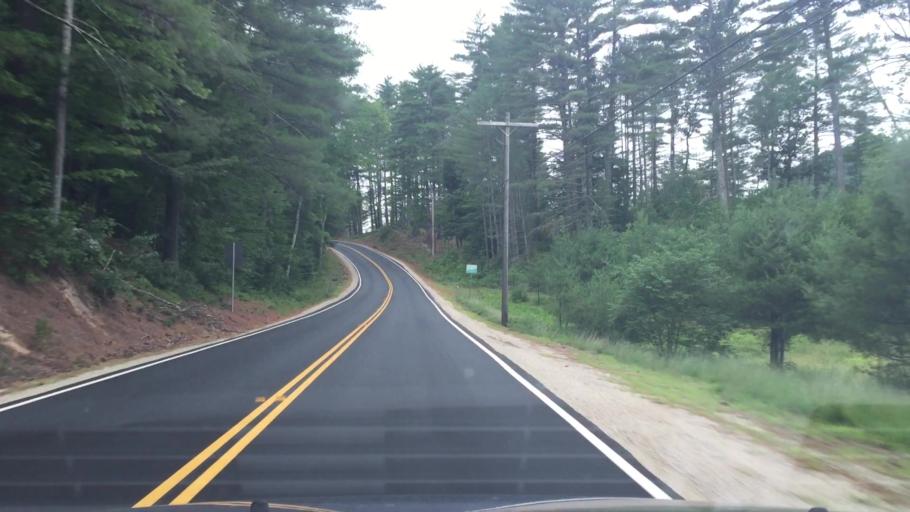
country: US
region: New Hampshire
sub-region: Carroll County
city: Freedom
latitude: 43.8489
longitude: -71.0921
